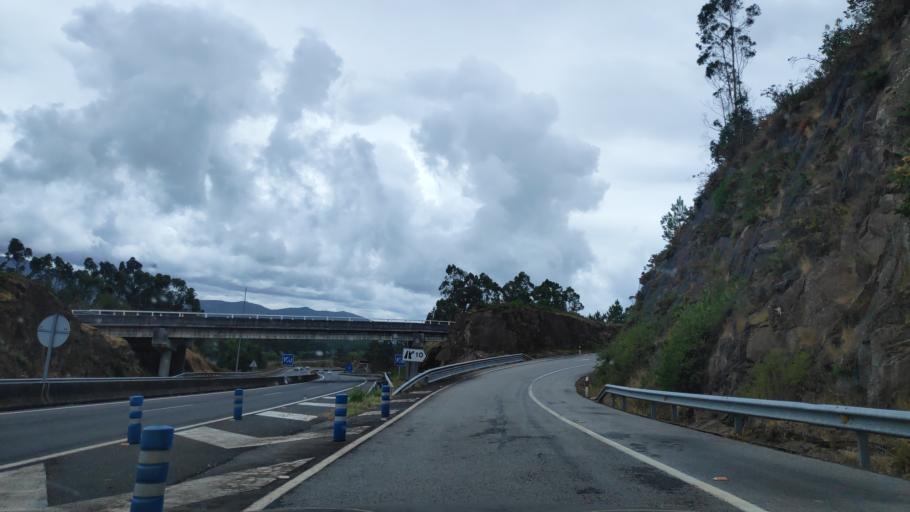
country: ES
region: Galicia
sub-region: Provincia de Pontevedra
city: Catoira
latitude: 42.6961
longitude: -8.7422
